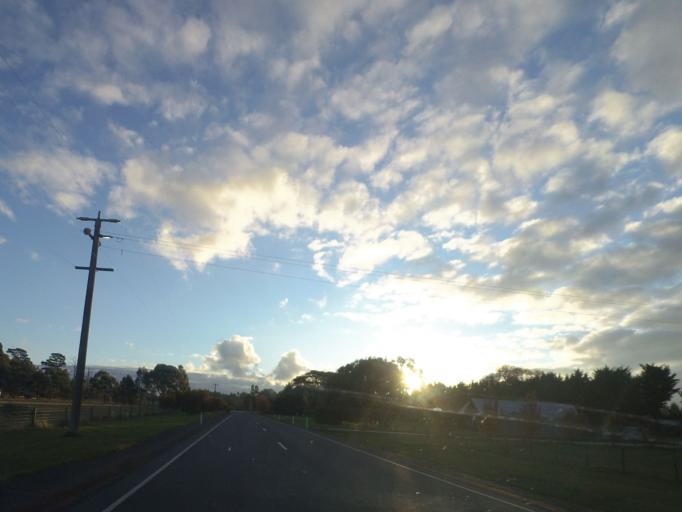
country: AU
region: Victoria
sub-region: Mount Alexander
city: Castlemaine
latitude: -37.2854
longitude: 144.5036
